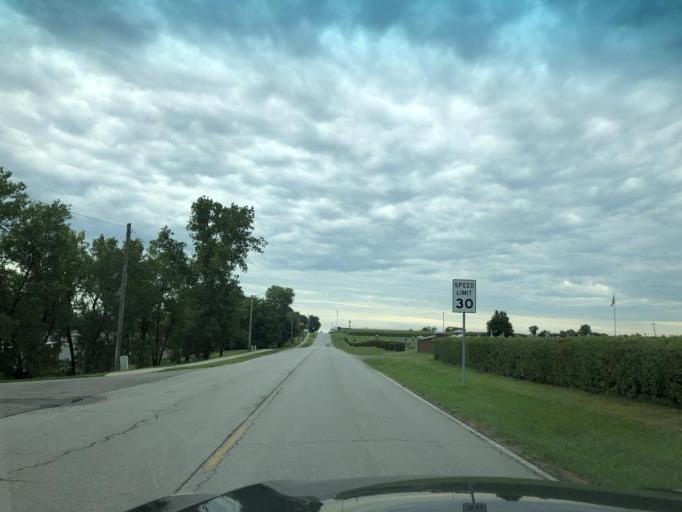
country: US
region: Missouri
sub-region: Saline County
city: Sweet Springs
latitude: 38.9704
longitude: -93.4153
